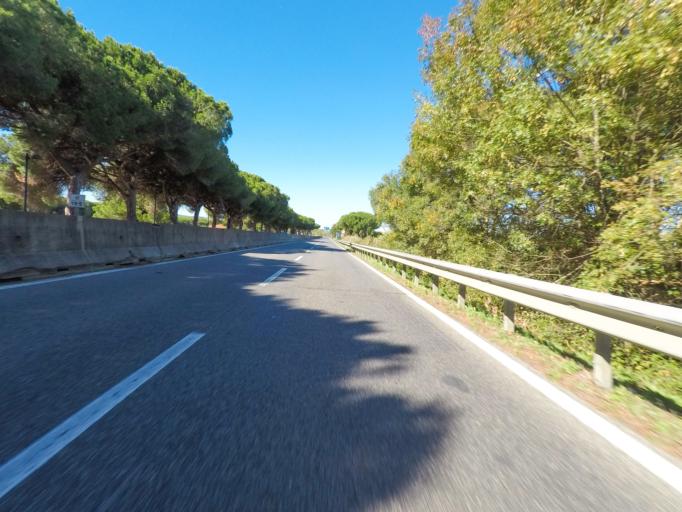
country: IT
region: Tuscany
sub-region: Provincia di Grosseto
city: Fonteblanda
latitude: 42.5406
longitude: 11.1810
